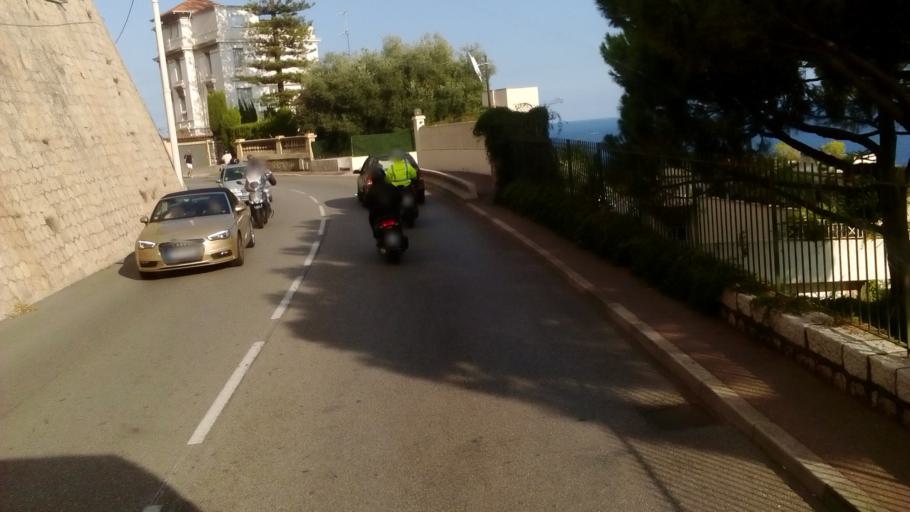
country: MC
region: Commune de Monaco
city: Saint-Roman
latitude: 43.7532
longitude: 7.4449
